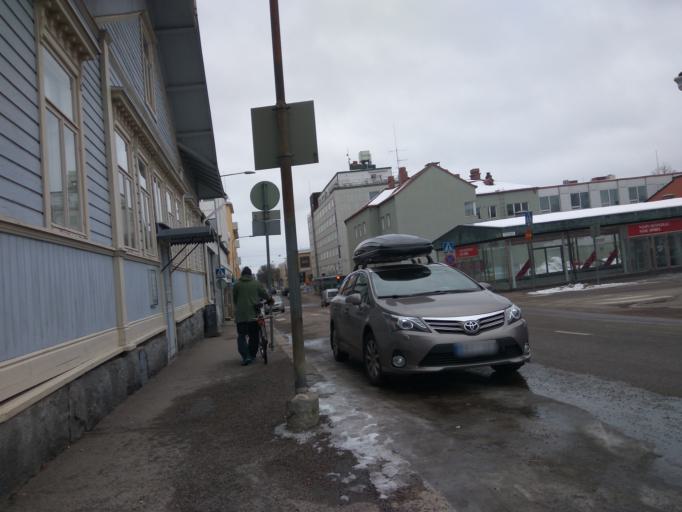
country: FI
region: Uusimaa
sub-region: Porvoo
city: Porvoo
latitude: 60.3955
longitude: 25.6632
